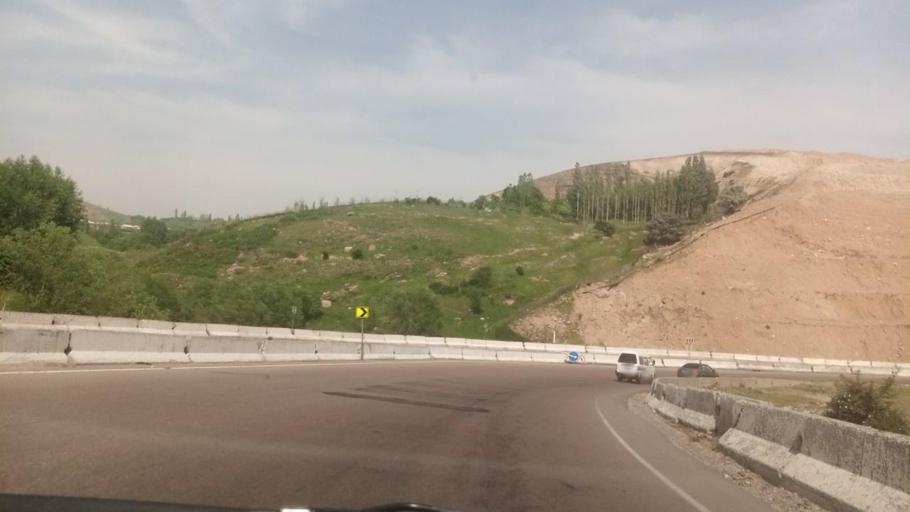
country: UZ
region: Toshkent
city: Angren
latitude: 41.0728
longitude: 70.2341
